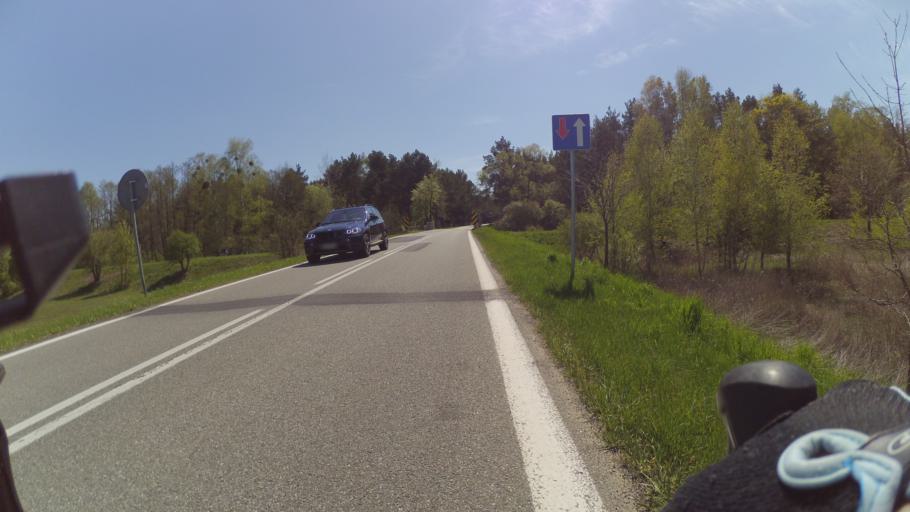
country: PL
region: Masovian Voivodeship
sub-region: Powiat plonski
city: Czerwinsk Nad Wisla
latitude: 52.3695
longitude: 20.3084
